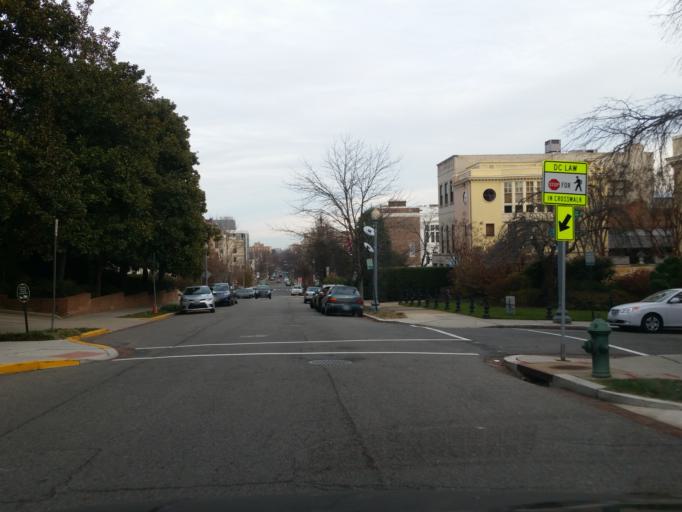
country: US
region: Washington, D.C.
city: Washington, D.C.
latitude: 38.9141
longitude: -77.0490
